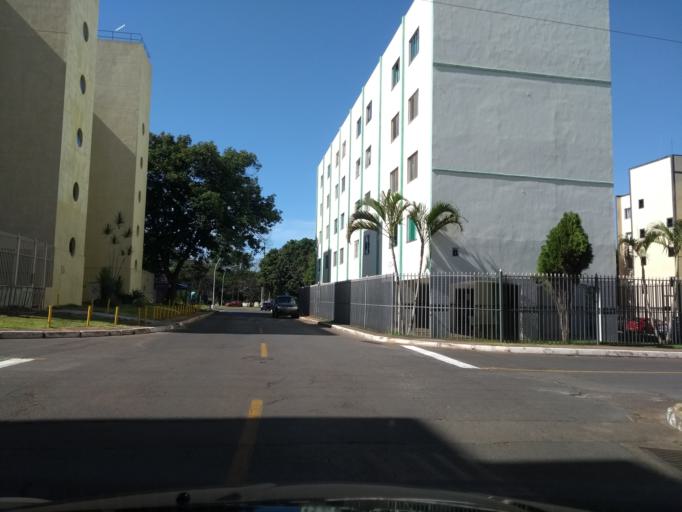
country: BR
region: Federal District
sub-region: Brasilia
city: Brasilia
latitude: -15.8006
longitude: -47.9413
